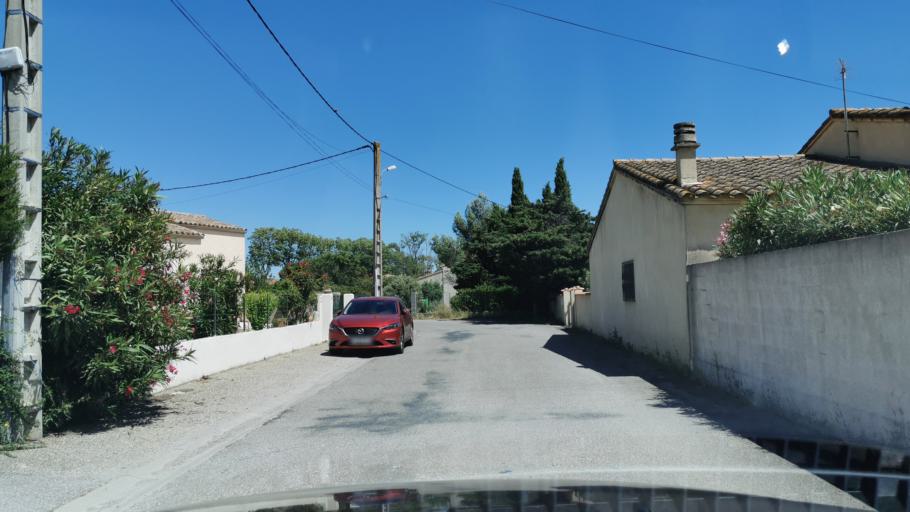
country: FR
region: Languedoc-Roussillon
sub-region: Departement de l'Aude
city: Canet
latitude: 43.2159
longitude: 2.8570
